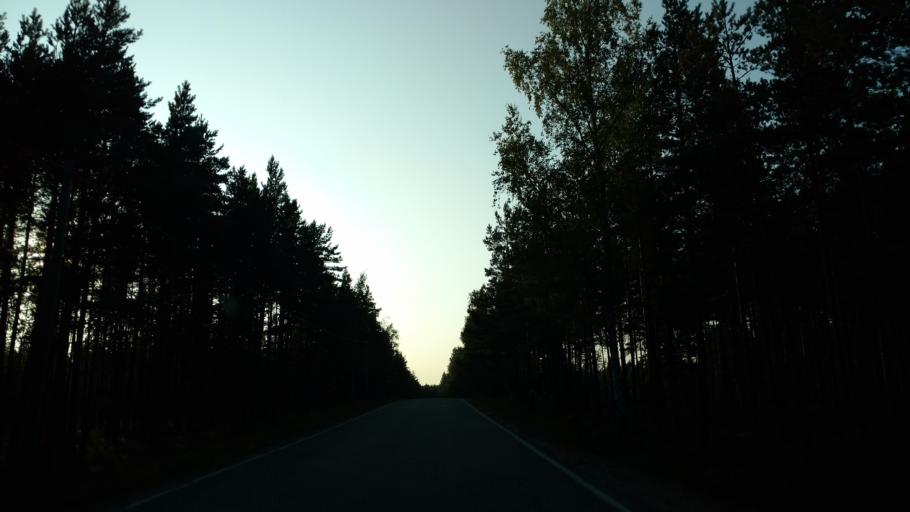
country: FI
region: Varsinais-Suomi
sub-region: Salo
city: Saerkisalo
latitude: 60.1994
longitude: 22.9381
